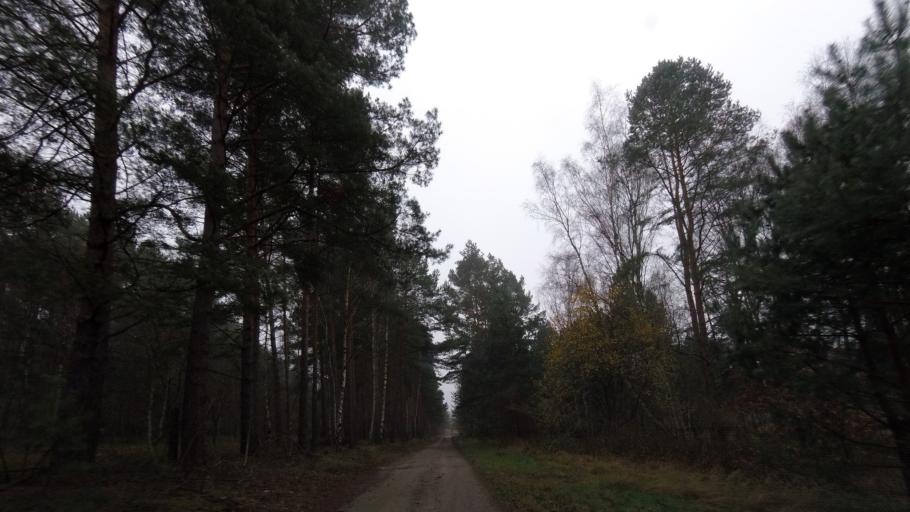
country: DE
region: Brandenburg
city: Treuenbrietzen
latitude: 52.0577
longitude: 12.8894
